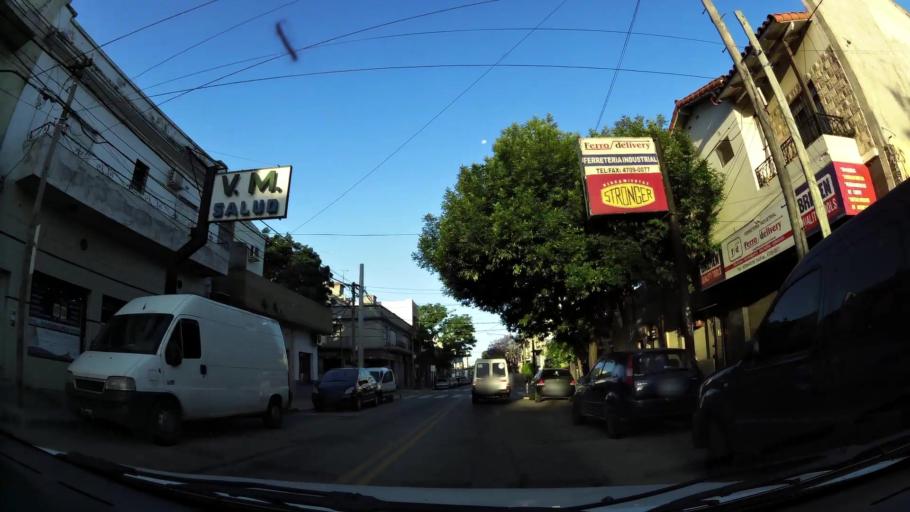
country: AR
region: Buenos Aires
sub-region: Partido de General San Martin
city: General San Martin
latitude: -34.5467
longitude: -58.5015
